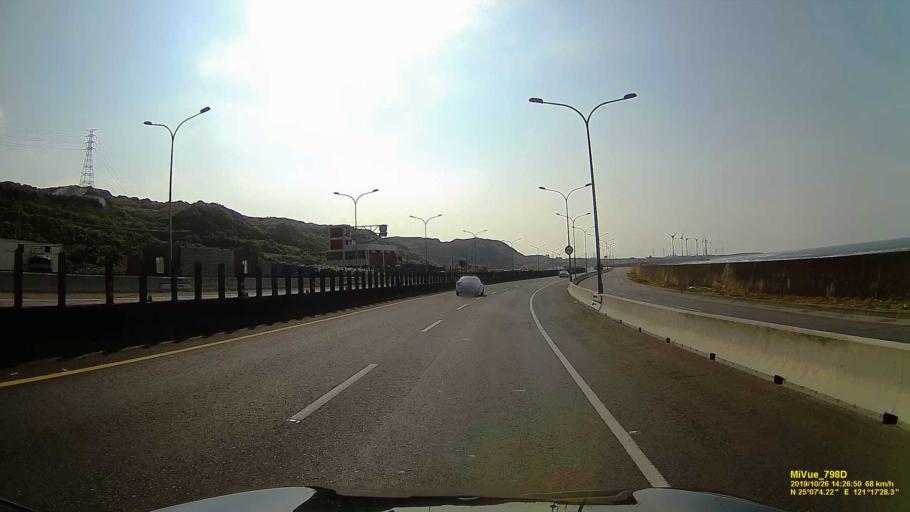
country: TW
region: Taiwan
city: Taoyuan City
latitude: 25.1176
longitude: 121.2905
